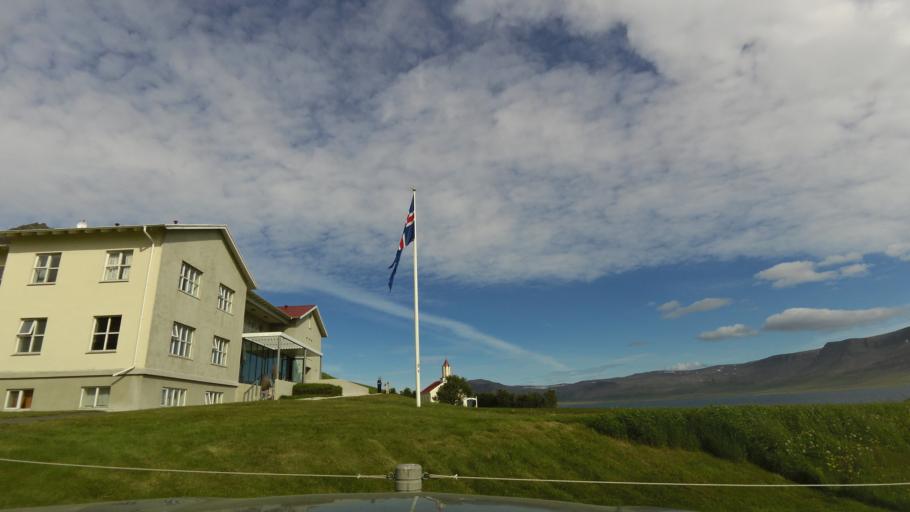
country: IS
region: Westfjords
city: Isafjoerdur
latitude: 65.7596
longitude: -23.4518
